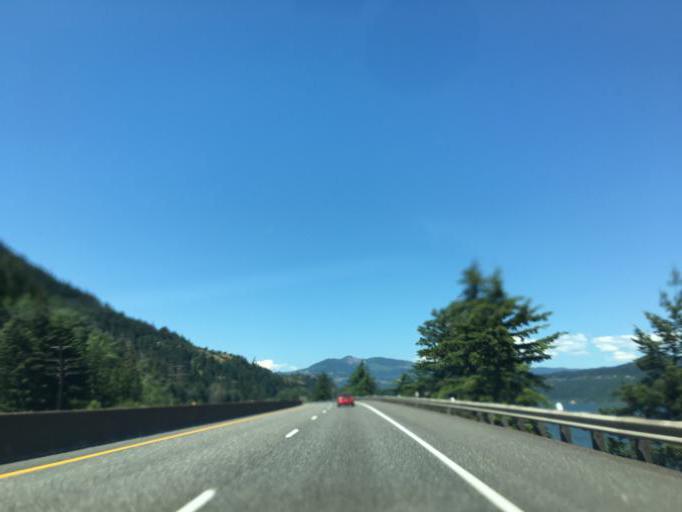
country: US
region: Washington
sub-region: Klickitat County
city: White Salmon
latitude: 45.6972
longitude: -121.4614
